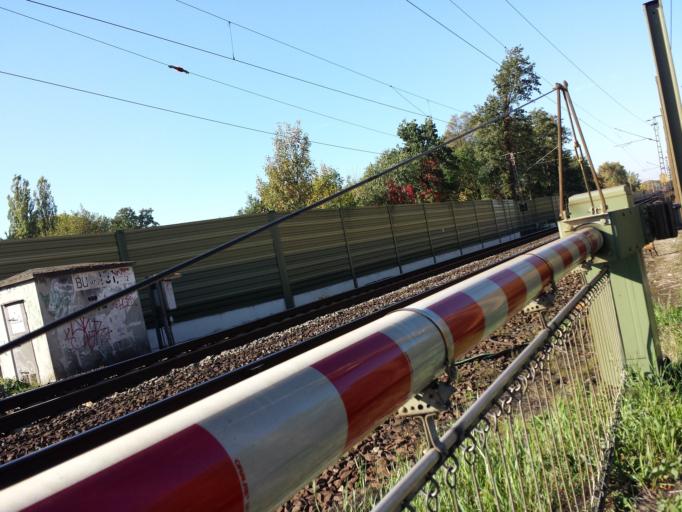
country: DE
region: Lower Saxony
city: Ritterhude
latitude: 53.1459
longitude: 8.7207
